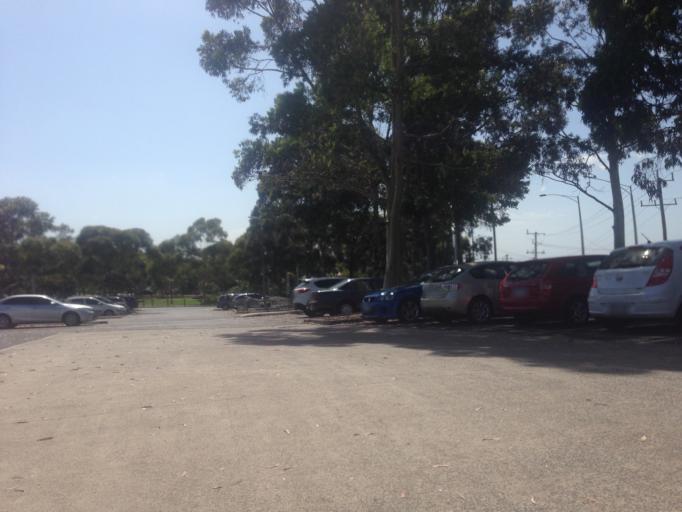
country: AU
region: Victoria
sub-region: Darebin
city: Northcote
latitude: -37.7696
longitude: 145.0024
